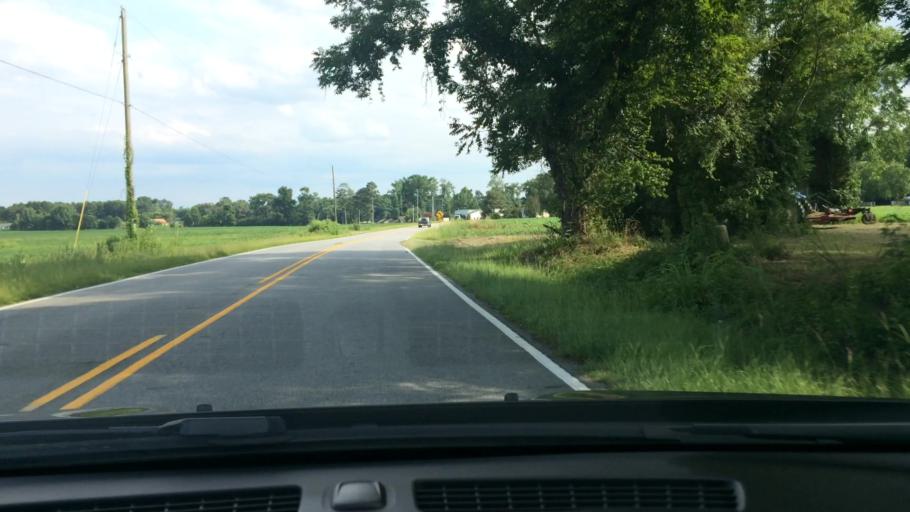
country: US
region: North Carolina
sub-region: Pitt County
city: Winterville
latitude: 35.4957
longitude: -77.3785
